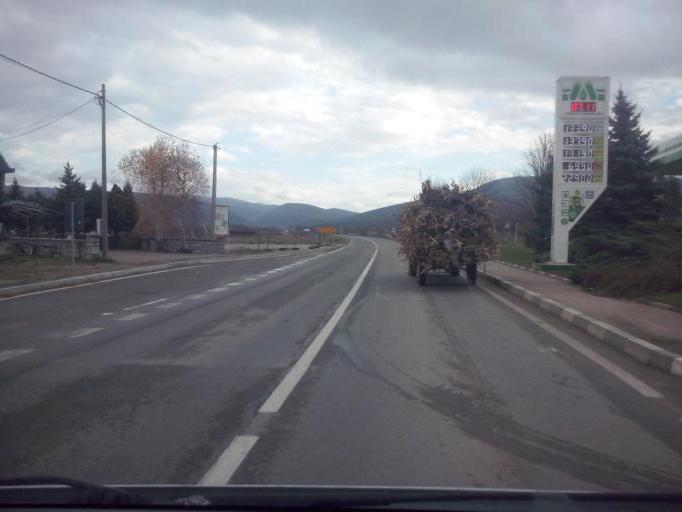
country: RS
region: Central Serbia
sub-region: Pomoravski Okrug
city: Paracin
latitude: 43.8551
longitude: 21.5584
